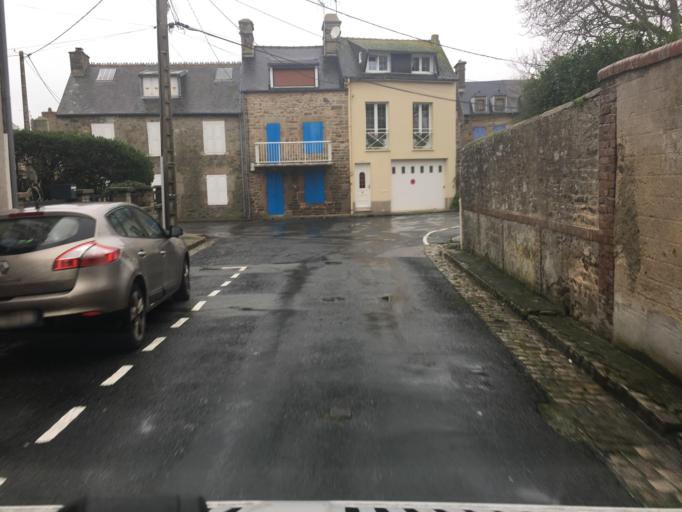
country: FR
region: Lower Normandy
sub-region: Departement de la Manche
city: Saint-Vaast-la-Hougue
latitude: 49.5851
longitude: -1.2632
